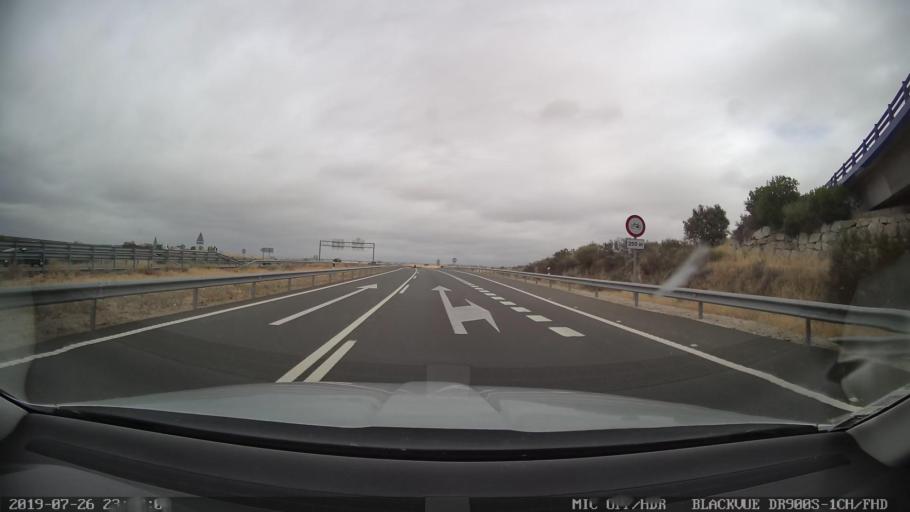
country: ES
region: Extremadura
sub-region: Provincia de Caceres
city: Trujillo
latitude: 39.4965
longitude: -5.8416
